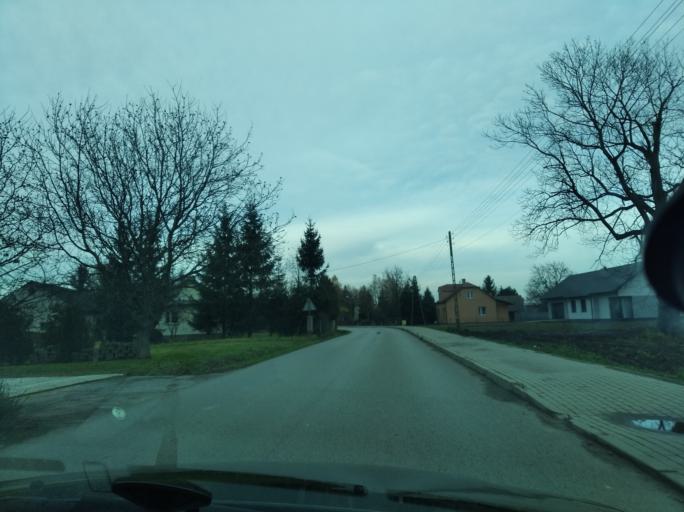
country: PL
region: Subcarpathian Voivodeship
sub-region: Powiat przeworski
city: Grzeska
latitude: 50.0810
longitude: 22.4545
